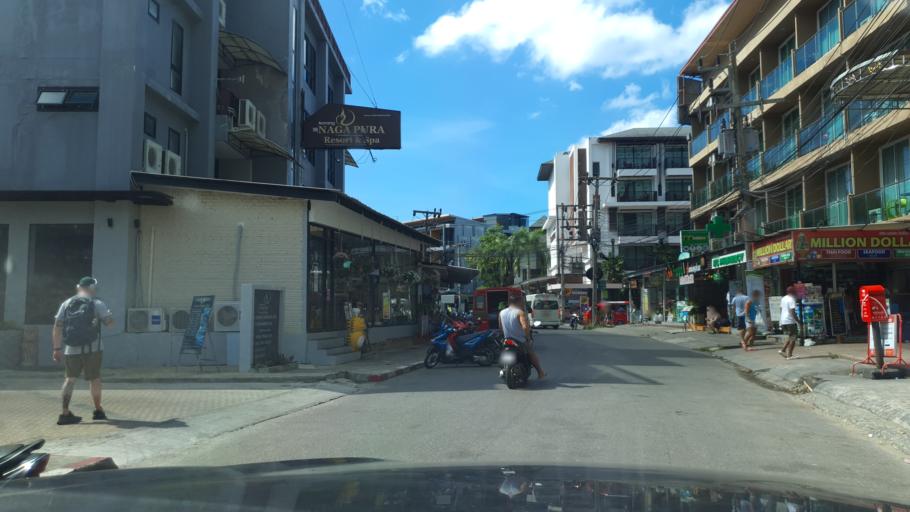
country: TH
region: Phangnga
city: Ban Ao Nang
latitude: 8.0412
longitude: 98.8180
